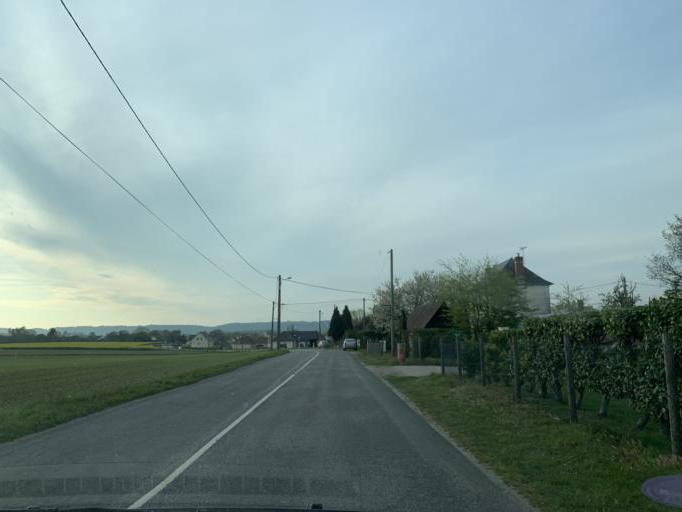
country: FR
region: Haute-Normandie
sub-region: Departement de la Seine-Maritime
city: La Mailleraye-sur-Seine
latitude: 49.5023
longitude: 0.7493
